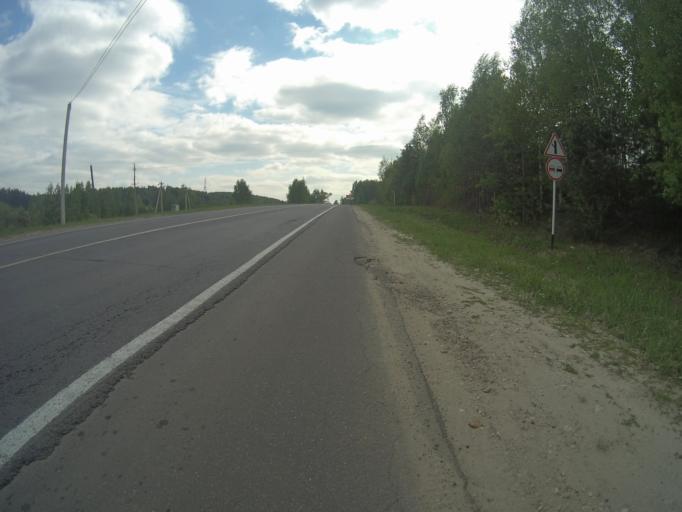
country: RU
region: Vladimir
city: Raduzhnyy
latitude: 56.0204
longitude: 40.3200
